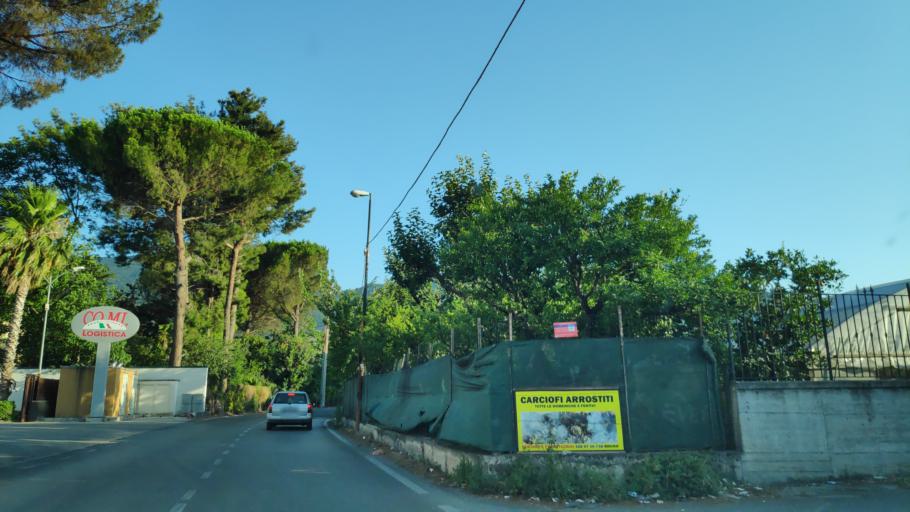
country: IT
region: Campania
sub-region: Provincia di Salerno
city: Pagani
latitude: 40.7546
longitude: 14.6158
